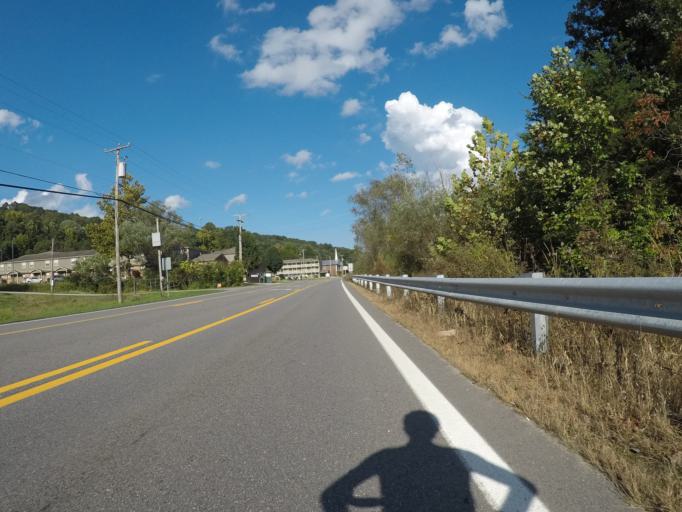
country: US
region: Ohio
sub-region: Lawrence County
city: Burlington
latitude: 38.3821
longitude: -82.5239
